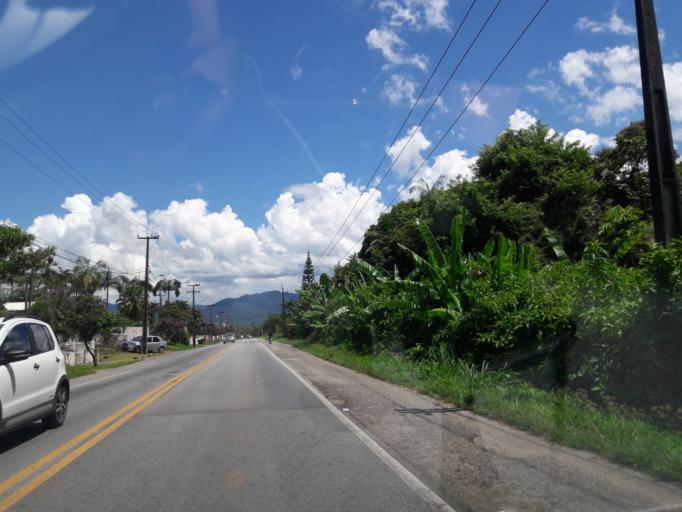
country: BR
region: Parana
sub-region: Antonina
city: Antonina
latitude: -25.4665
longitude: -48.8264
